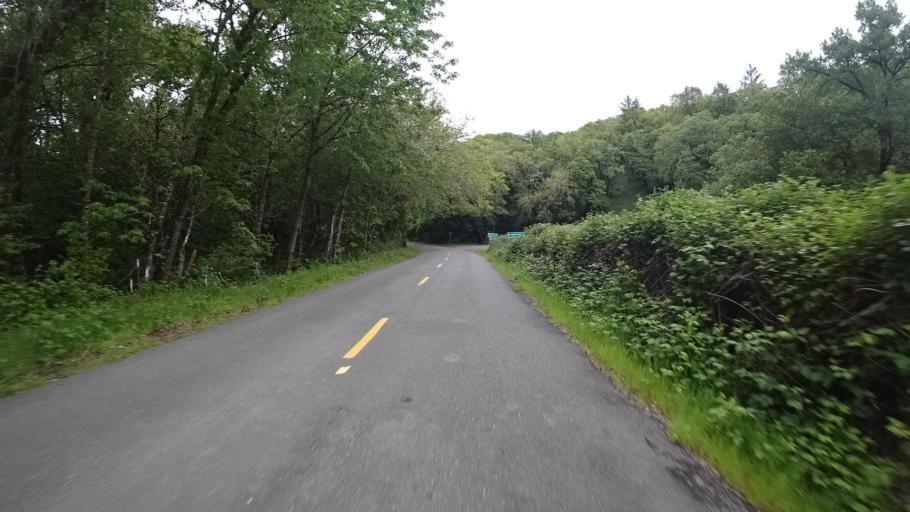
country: US
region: California
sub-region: Humboldt County
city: Blue Lake
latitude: 40.9697
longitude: -123.8405
